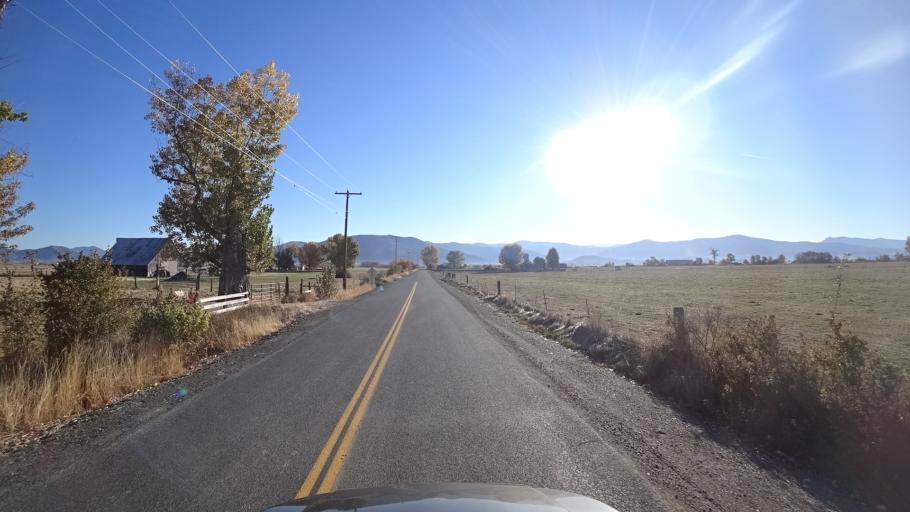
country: US
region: California
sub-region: Siskiyou County
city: Yreka
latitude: 41.5129
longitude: -122.8873
